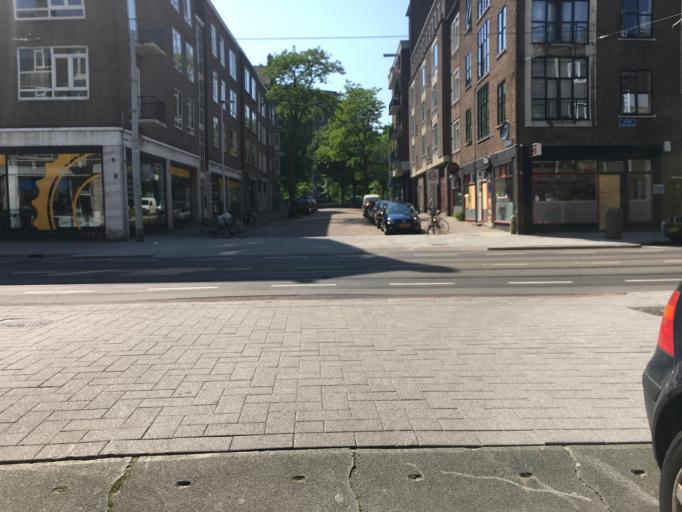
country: NL
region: South Holland
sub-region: Gemeente Rotterdam
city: Rotterdam
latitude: 51.9263
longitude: 4.4869
